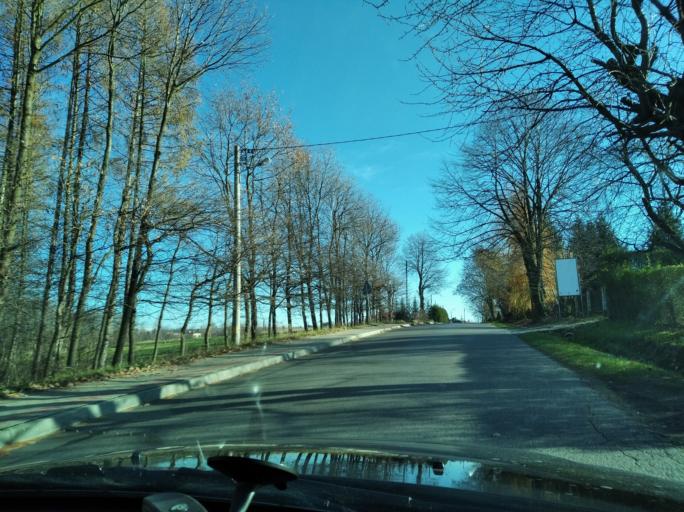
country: PL
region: Subcarpathian Voivodeship
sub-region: Powiat rzeszowski
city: Lutoryz
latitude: 49.9808
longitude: 21.9205
